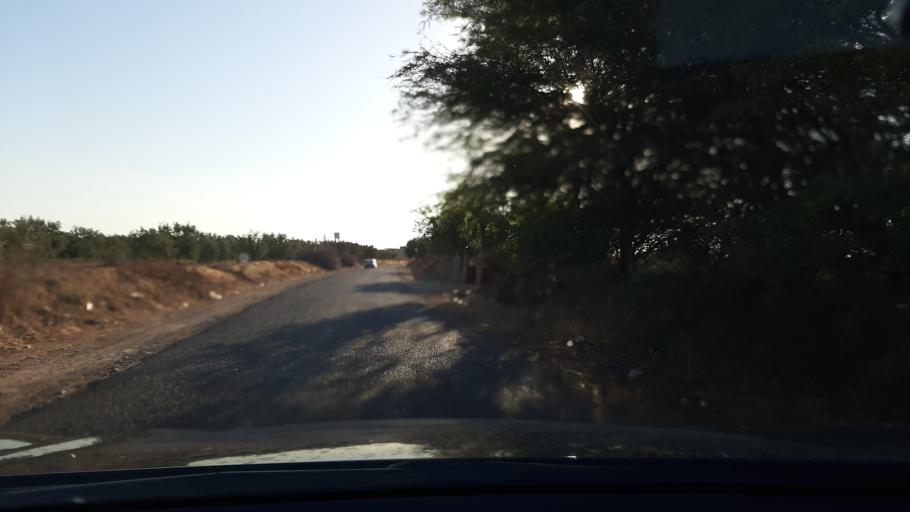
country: TN
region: Qabis
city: Matmata
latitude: 33.6175
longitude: 10.2540
